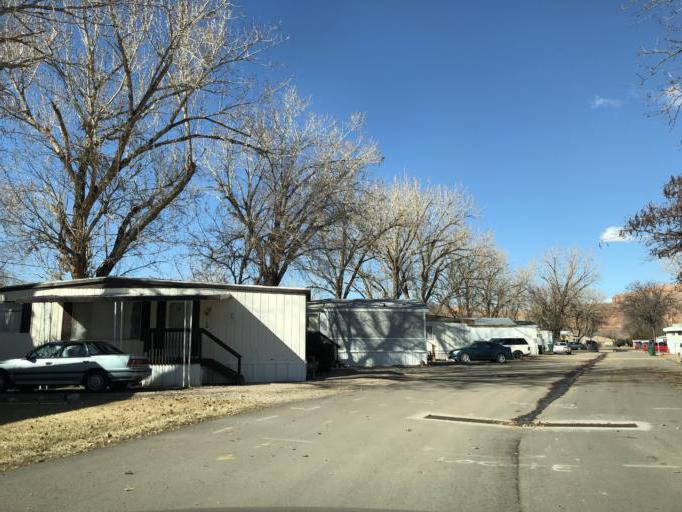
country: US
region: Utah
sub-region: Grand County
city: Moab
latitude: 38.5766
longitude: -109.5654
